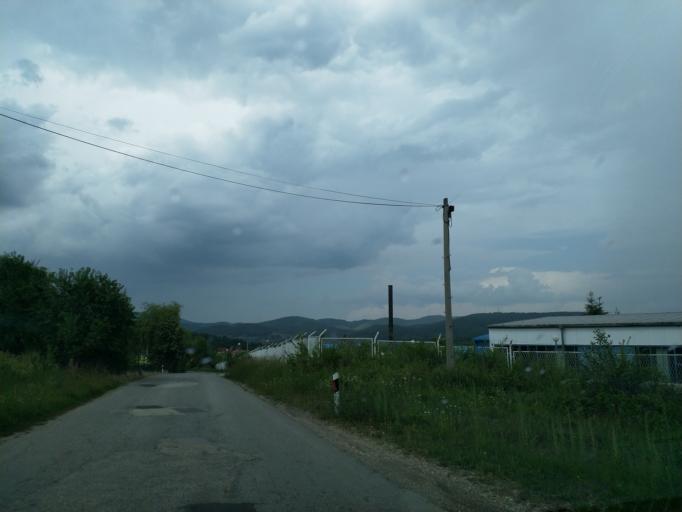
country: RS
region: Central Serbia
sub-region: Borski Okrug
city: Bor
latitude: 43.9974
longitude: 21.9788
